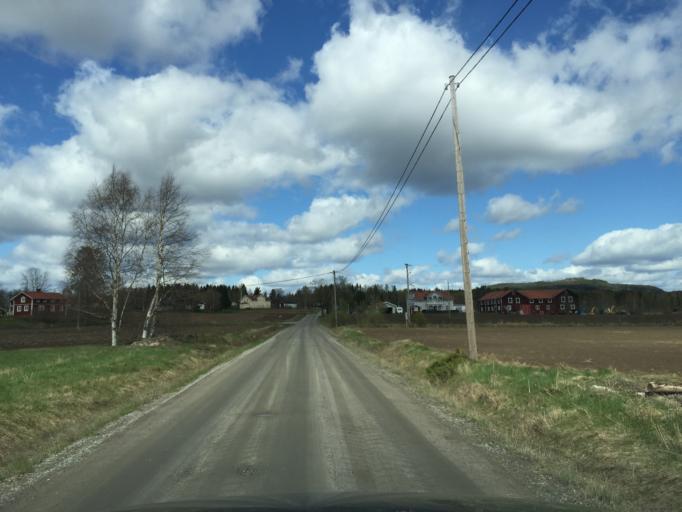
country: SE
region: Gaevleborg
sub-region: Bollnas Kommun
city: Arbra
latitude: 61.5159
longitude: 16.3540
